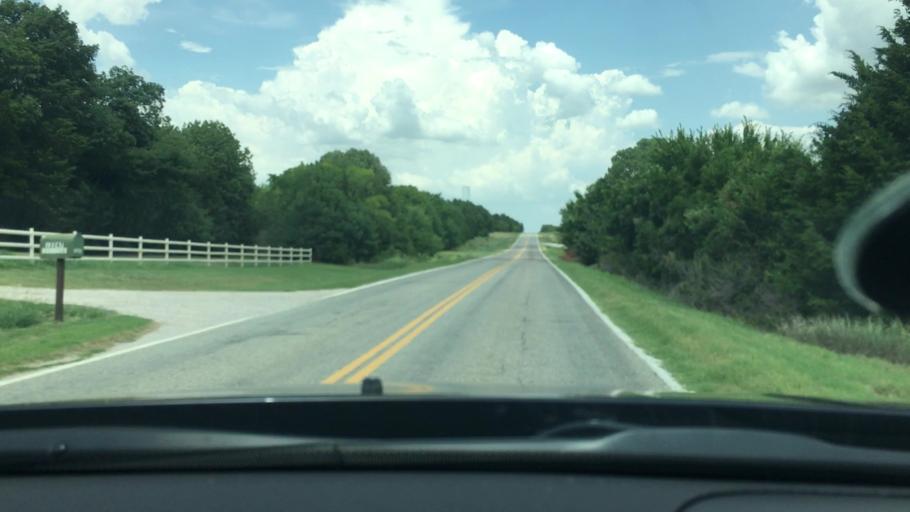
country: US
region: Oklahoma
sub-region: Marshall County
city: Oakland
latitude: 34.0017
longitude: -96.8805
